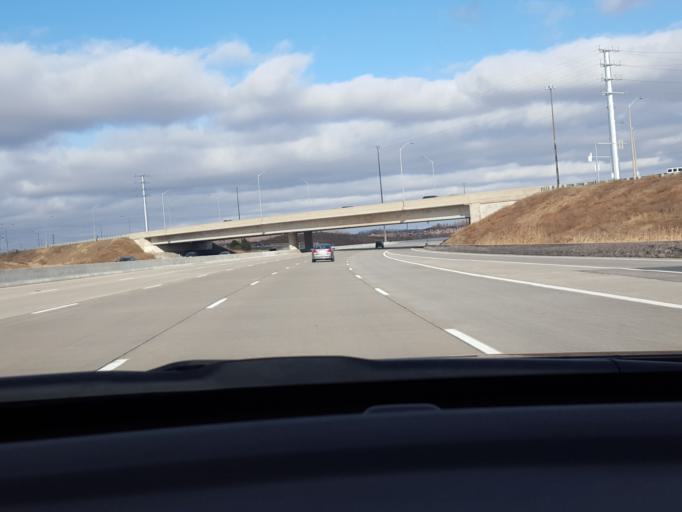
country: CA
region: Ontario
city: Concord
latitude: 43.8161
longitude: -79.4782
